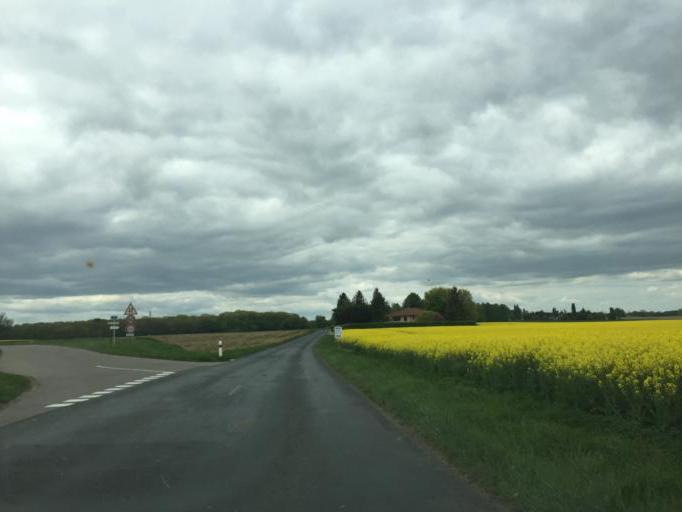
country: FR
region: Rhone-Alpes
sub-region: Departement de l'Ain
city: Saint-Andre-de-Corcy
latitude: 45.9343
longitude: 4.9495
